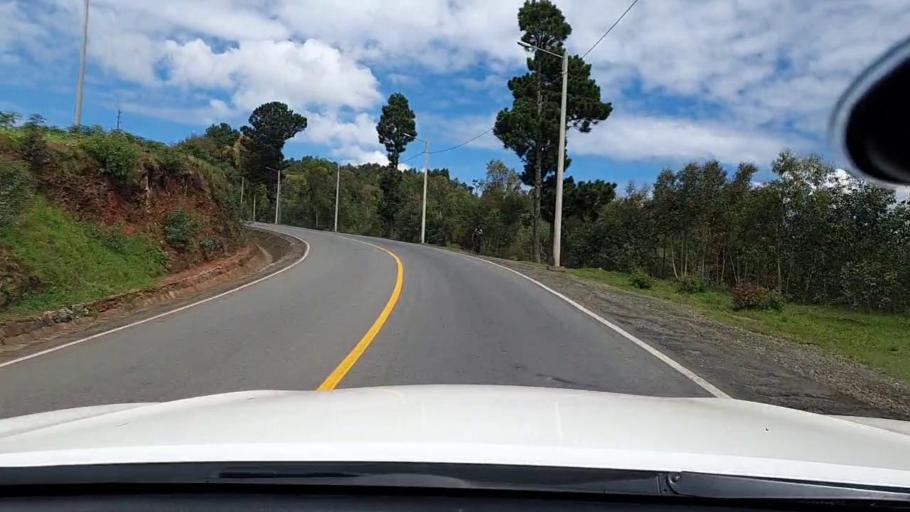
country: RW
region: Kigali
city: Kigali
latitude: -1.8288
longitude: 29.9493
